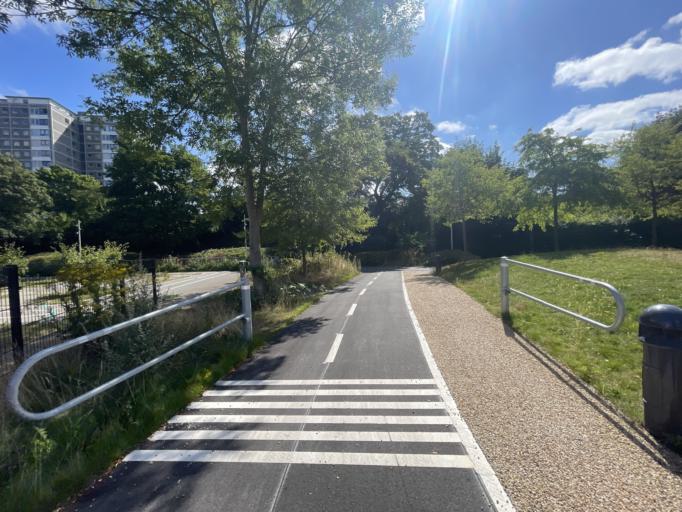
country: DK
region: Capital Region
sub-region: Kobenhavn
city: Vanlose
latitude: 55.6693
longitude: 12.5033
